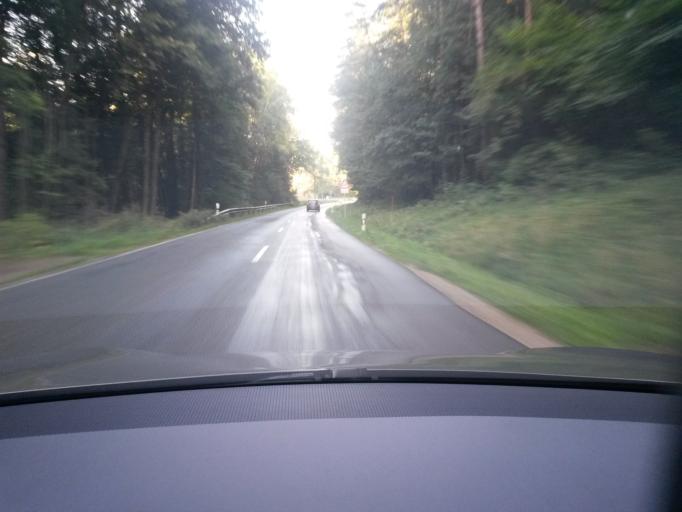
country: DE
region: Bavaria
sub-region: Upper Palatinate
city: Hohenfels
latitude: 49.1913
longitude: 11.8380
